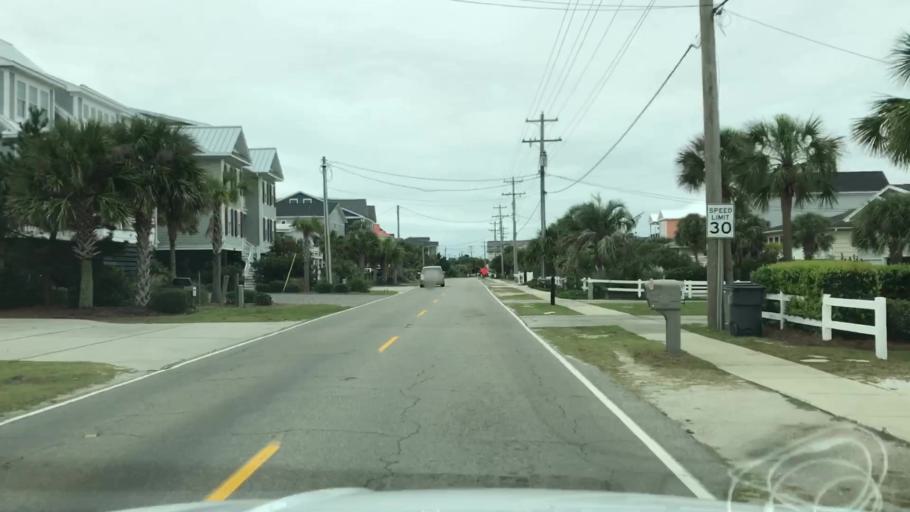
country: US
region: South Carolina
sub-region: Georgetown County
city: Murrells Inlet
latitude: 33.5561
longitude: -79.0161
